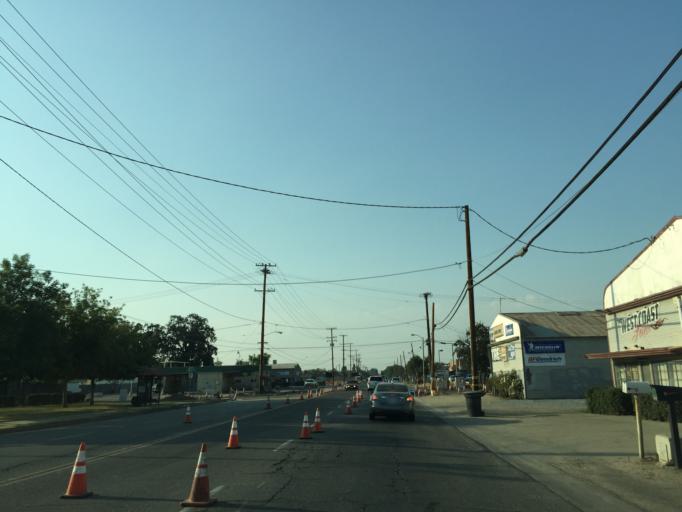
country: US
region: California
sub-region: Tulare County
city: Visalia
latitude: 36.3376
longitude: -119.2788
